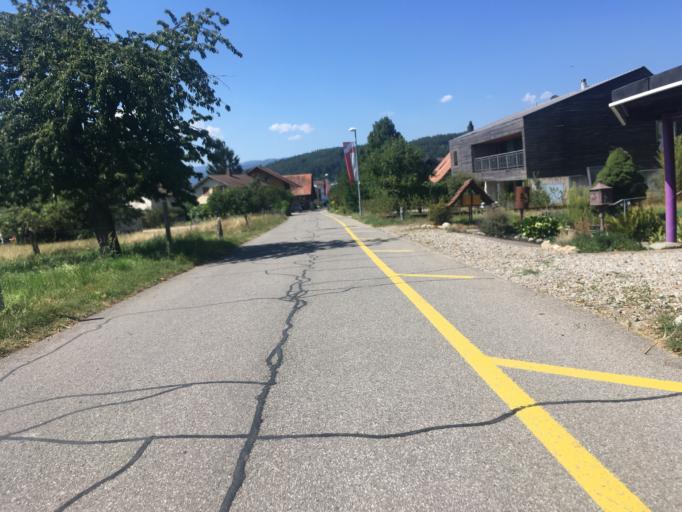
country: CH
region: Bern
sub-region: Seeland District
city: Grossaffoltern
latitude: 47.1100
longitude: 7.3604
